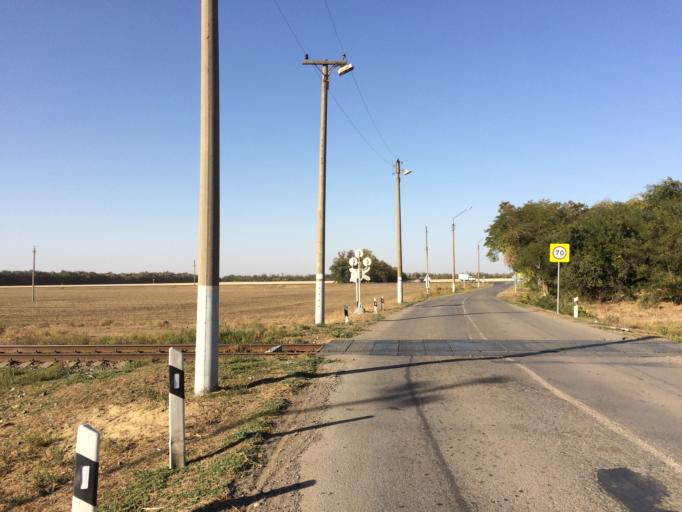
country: RU
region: Rostov
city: Tselina
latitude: 46.5282
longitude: 41.1878
